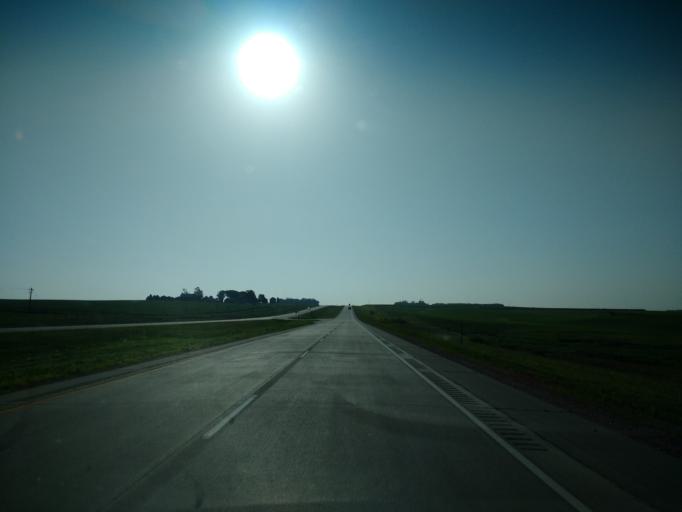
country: US
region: Iowa
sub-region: Ida County
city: Holstein
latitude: 42.4744
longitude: -95.6060
